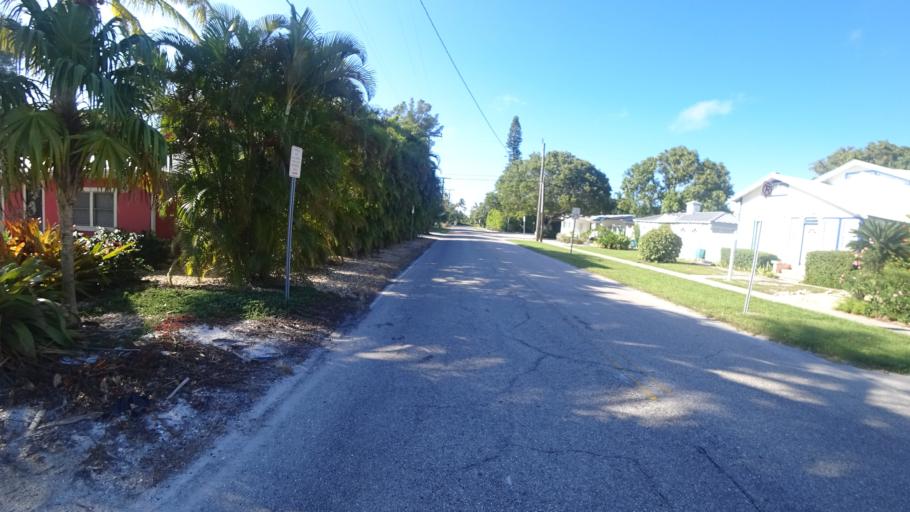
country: US
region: Florida
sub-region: Manatee County
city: Anna Maria
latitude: 27.5274
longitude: -82.7376
